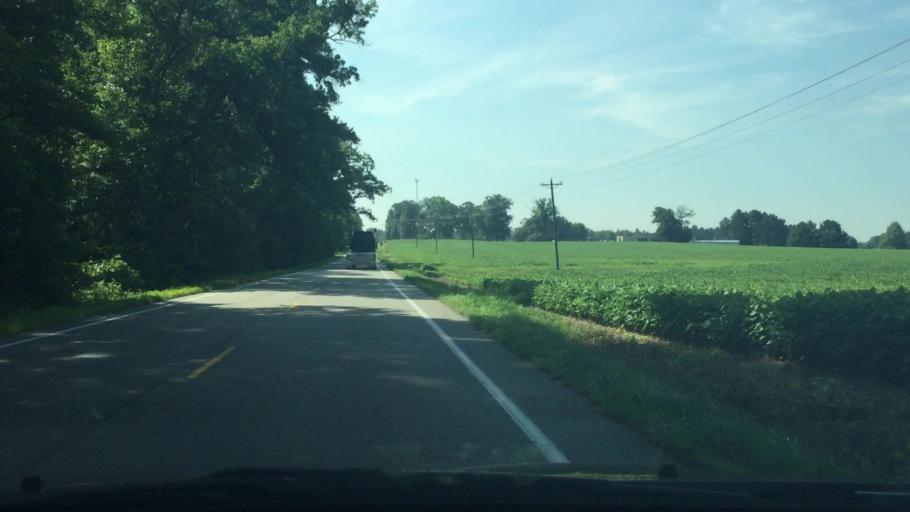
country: US
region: Virginia
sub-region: Sussex County
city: Sussex
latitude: 37.0421
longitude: -77.3112
